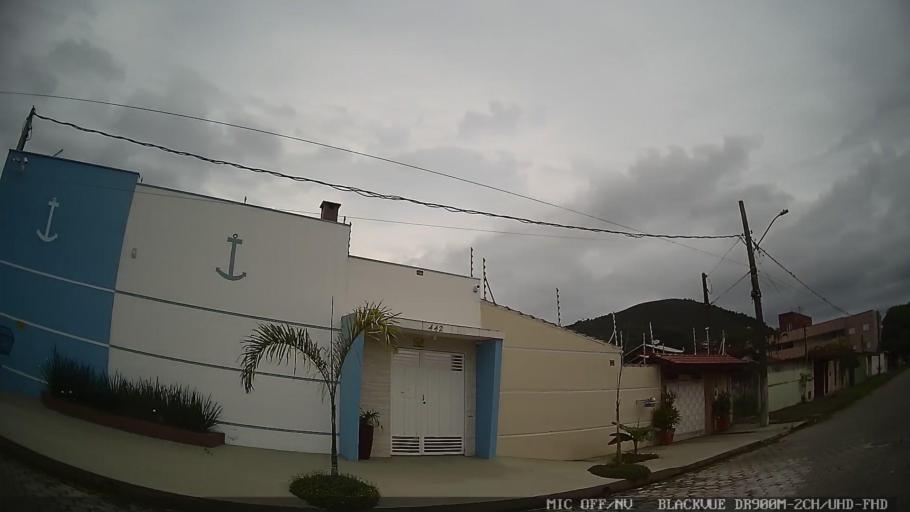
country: BR
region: Sao Paulo
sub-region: Caraguatatuba
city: Caraguatatuba
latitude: -23.6202
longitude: -45.3800
